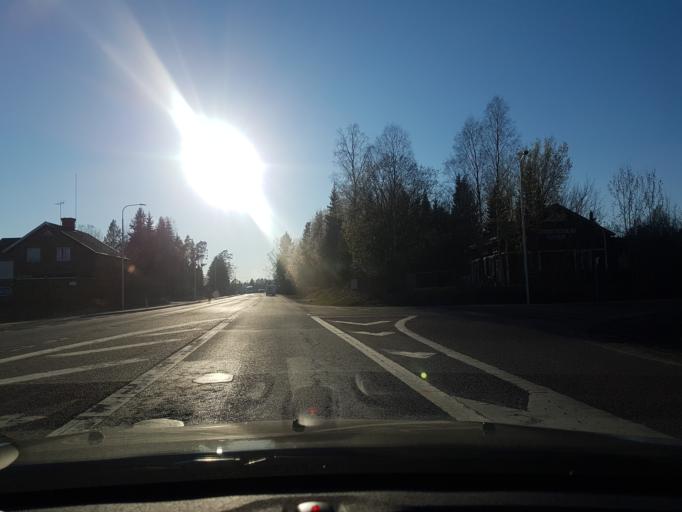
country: SE
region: Uppsala
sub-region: Heby Kommun
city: Morgongava
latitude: 59.9364
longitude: 16.9447
